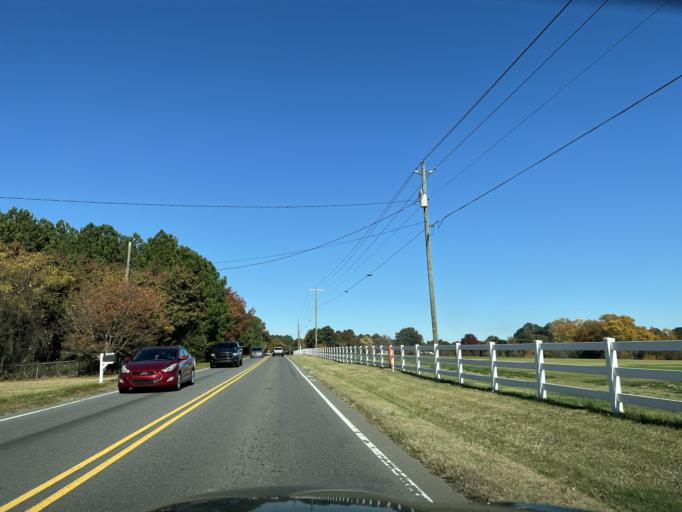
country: US
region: North Carolina
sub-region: Wake County
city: West Raleigh
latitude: 35.7391
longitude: -78.6813
